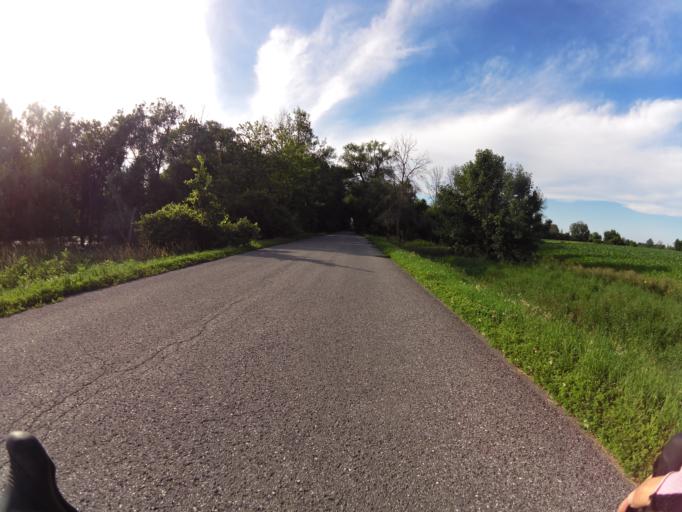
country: CA
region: Ontario
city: Bells Corners
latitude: 45.2267
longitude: -75.8058
